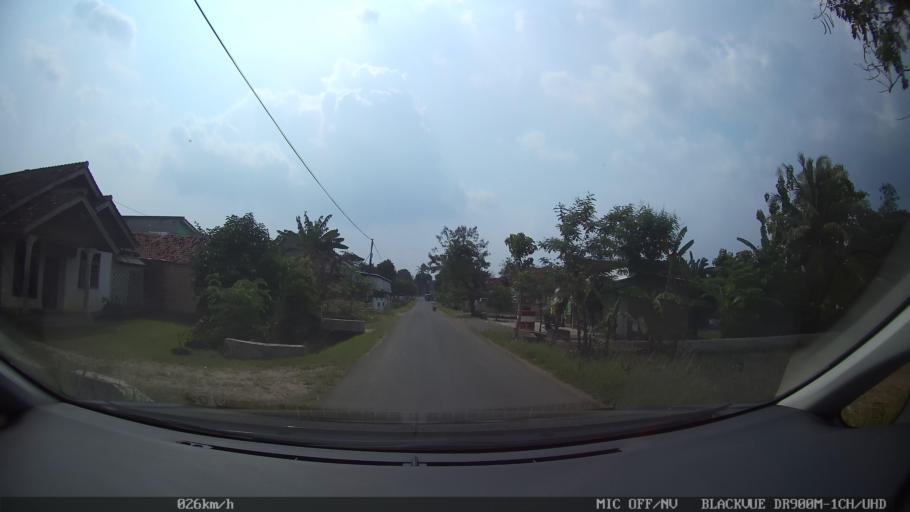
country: ID
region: Lampung
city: Gadingrejo
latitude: -5.3549
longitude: 105.0373
